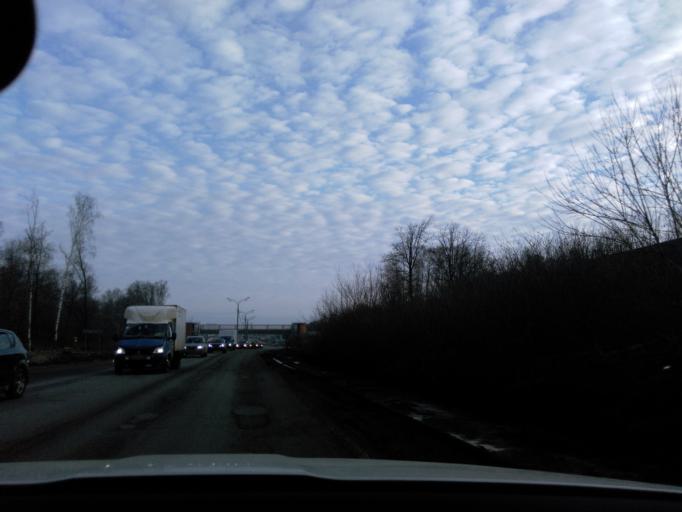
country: RU
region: Moscow
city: Businovo
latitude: 55.9055
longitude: 37.4930
